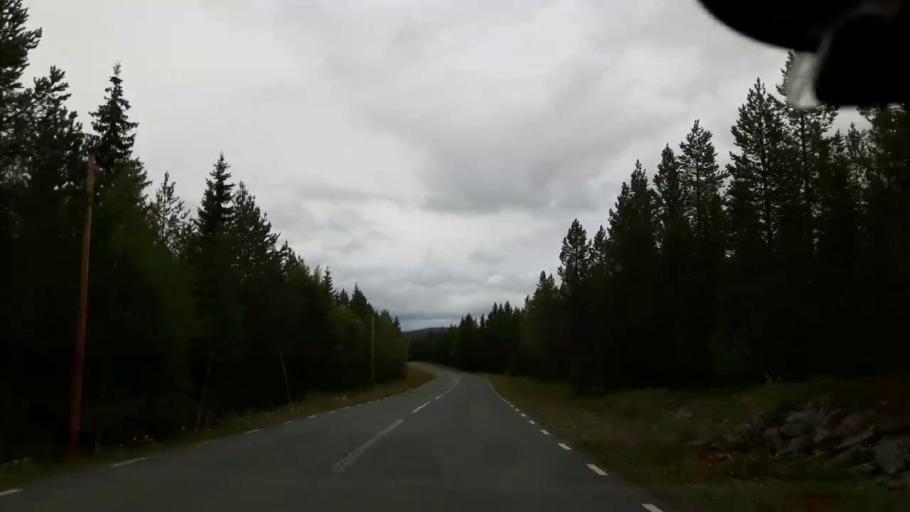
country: SE
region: Jaemtland
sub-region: Krokoms Kommun
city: Valla
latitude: 63.6681
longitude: 13.8604
